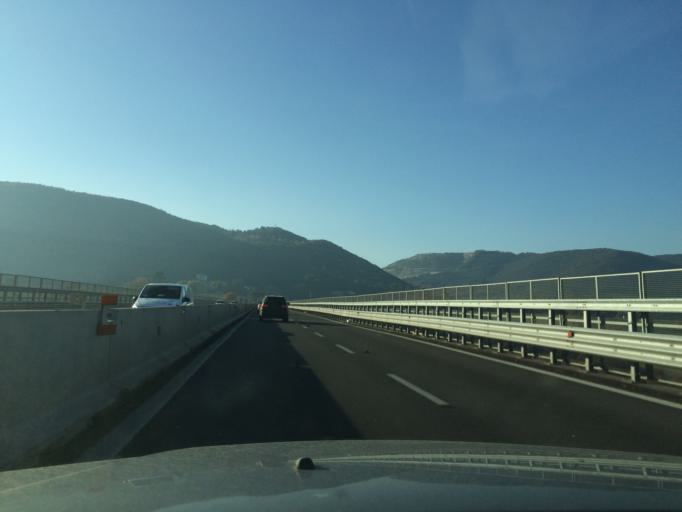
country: IT
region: Umbria
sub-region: Provincia di Terni
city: Narni Scalo
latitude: 42.5403
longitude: 12.5111
